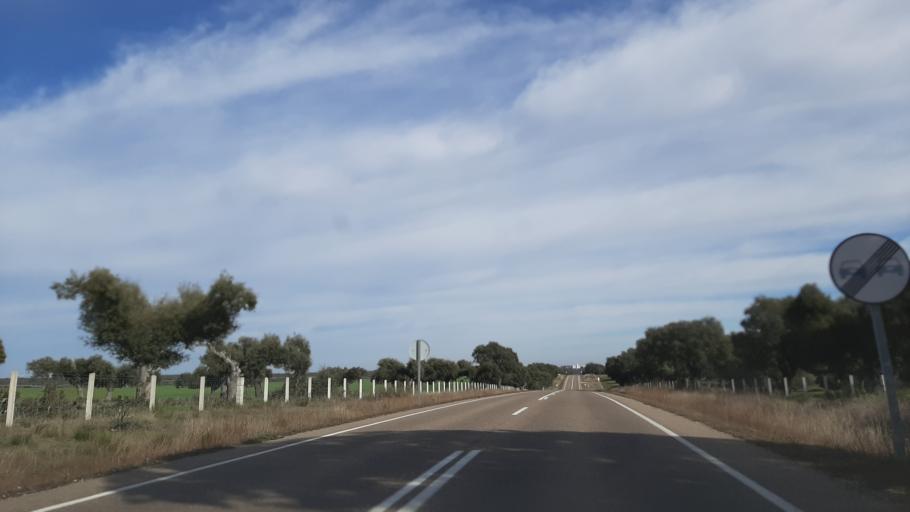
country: ES
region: Castille and Leon
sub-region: Provincia de Salamanca
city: Anover de Tormes
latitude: 41.0895
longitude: -5.9405
